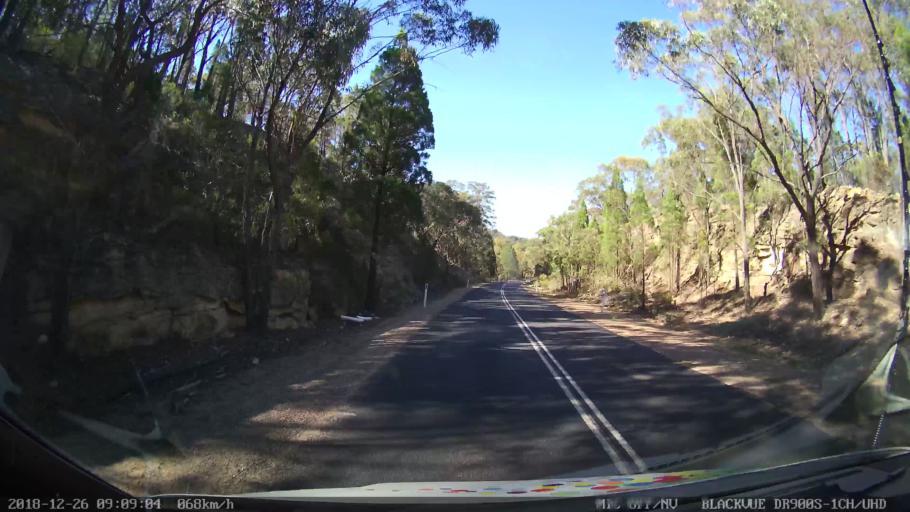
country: AU
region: New South Wales
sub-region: Mid-Western Regional
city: Kandos
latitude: -32.7213
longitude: 149.9991
